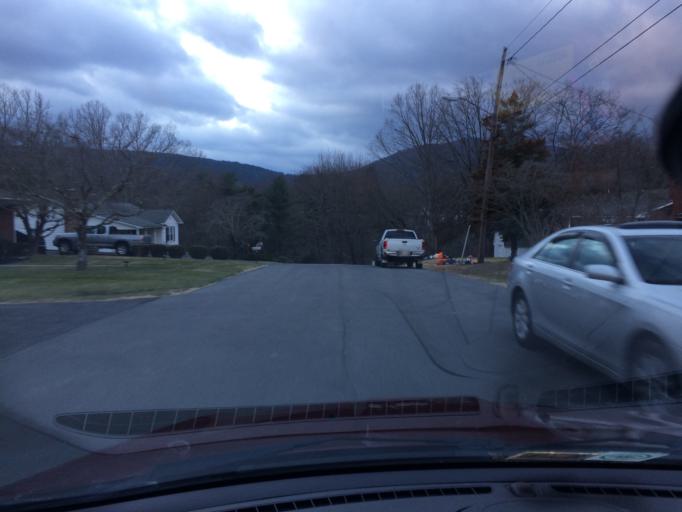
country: US
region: Virginia
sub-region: Alleghany County
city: Clifton Forge
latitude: 37.8218
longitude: -79.8189
